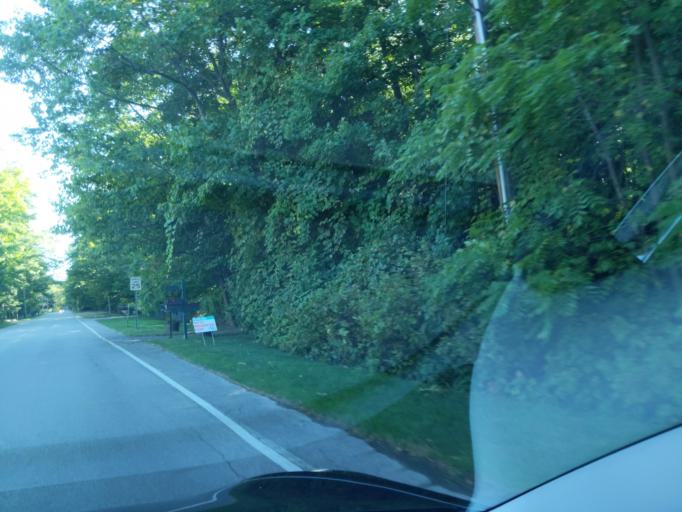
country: US
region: Michigan
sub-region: Antrim County
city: Elk Rapids
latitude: 44.8896
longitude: -85.4223
